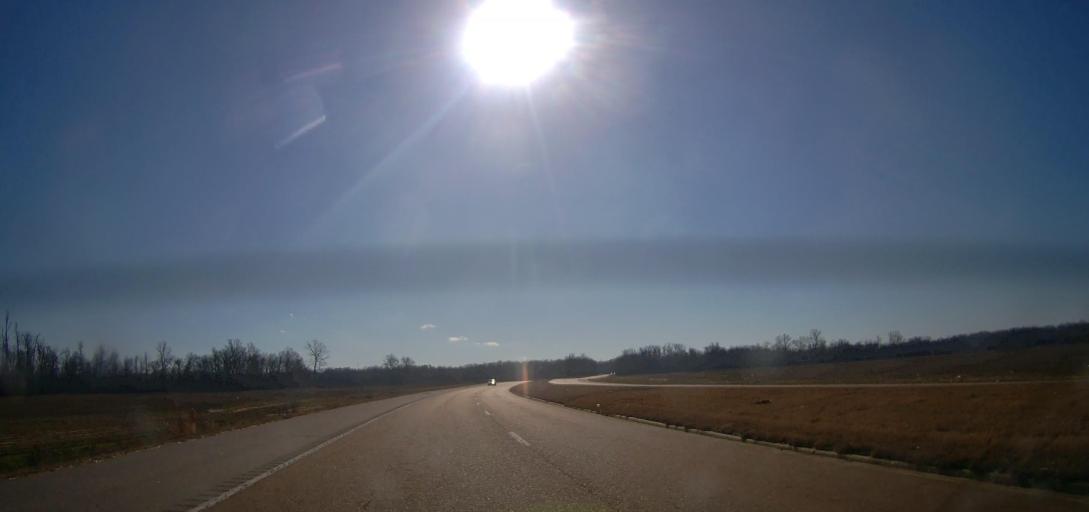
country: US
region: Tennessee
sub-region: Shelby County
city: Millington
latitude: 35.2877
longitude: -89.8825
